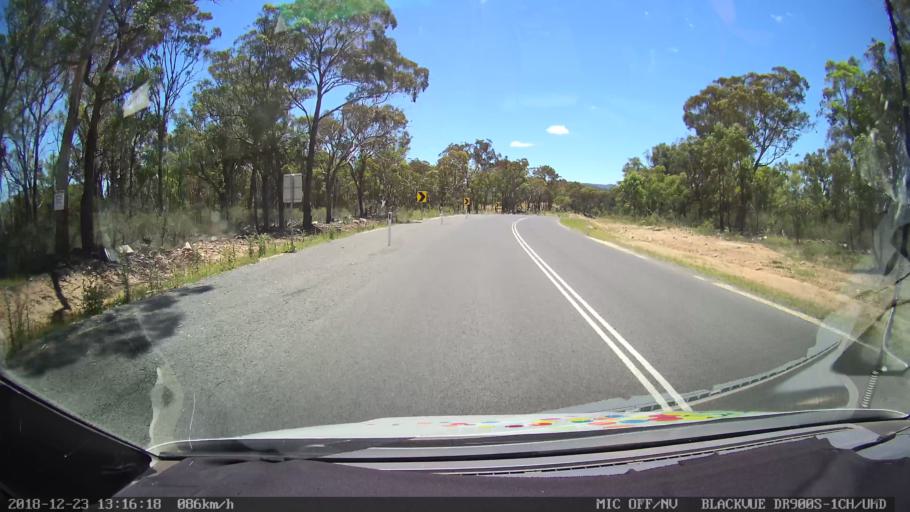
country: AU
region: New South Wales
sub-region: Armidale Dumaresq
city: Armidale
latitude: -30.5019
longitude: 151.5008
